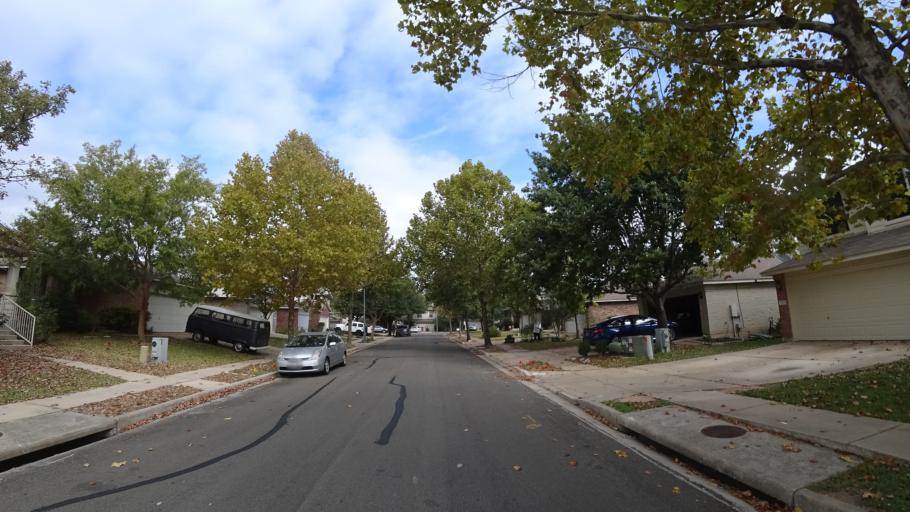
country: US
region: Texas
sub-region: Travis County
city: Manchaca
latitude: 30.1543
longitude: -97.8392
